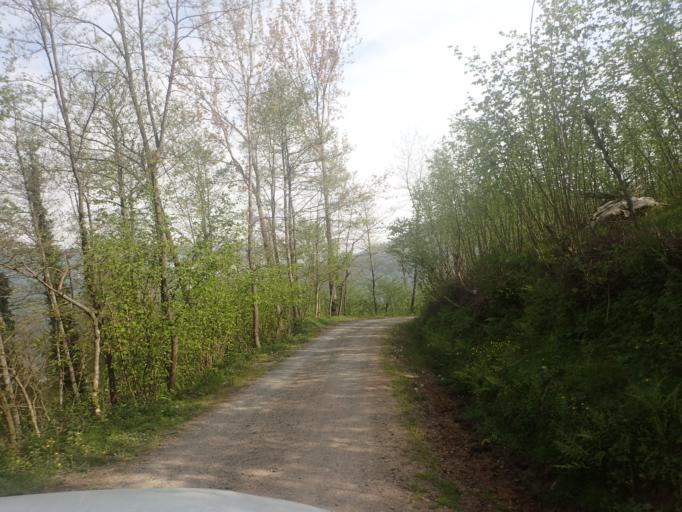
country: TR
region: Ordu
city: Catalpinar
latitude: 40.8904
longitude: 37.4792
